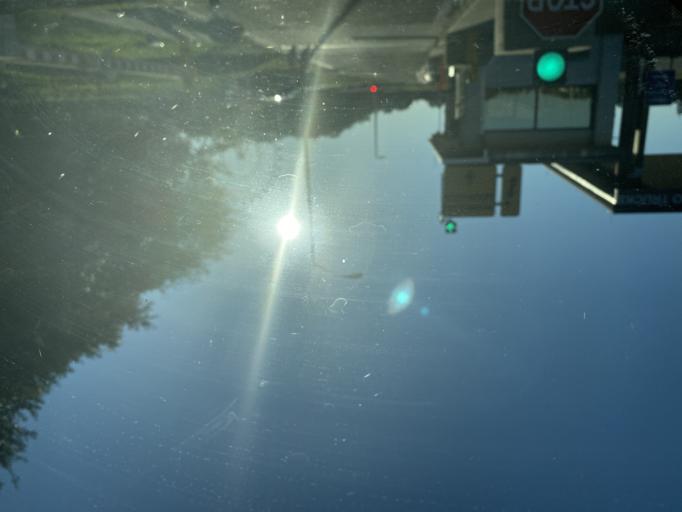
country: US
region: Florida
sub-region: Orange County
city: Tangelo Park
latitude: 28.4463
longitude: -81.4627
